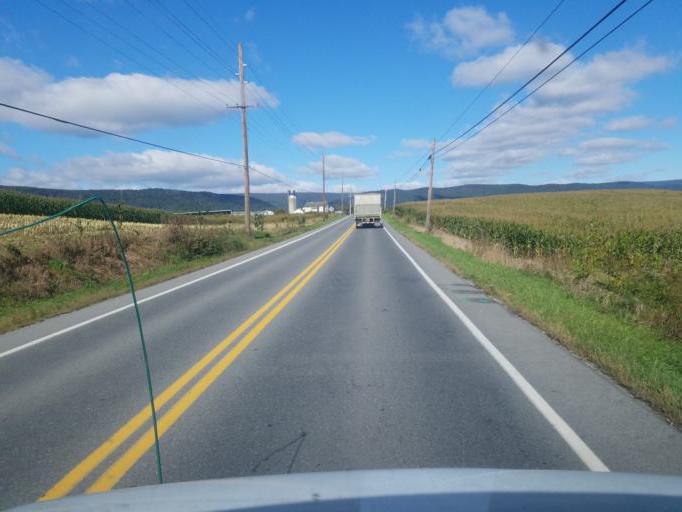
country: US
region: Pennsylvania
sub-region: Franklin County
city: Mercersburg
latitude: 39.8437
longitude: -77.9151
